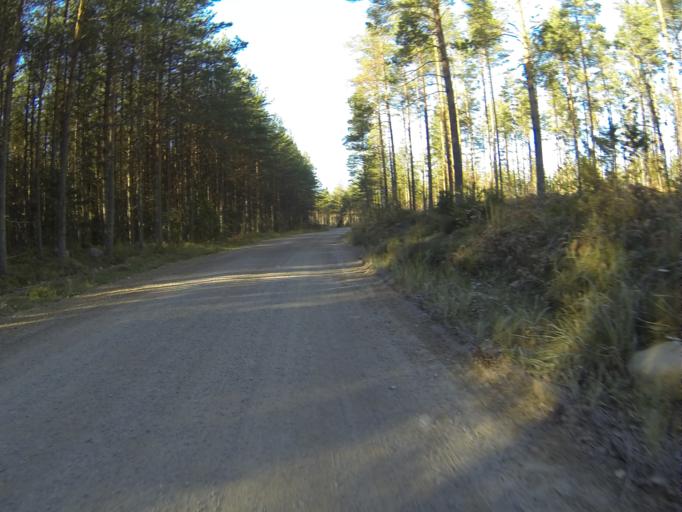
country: FI
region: Varsinais-Suomi
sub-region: Salo
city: Saerkisalo
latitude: 60.2260
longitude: 22.9830
